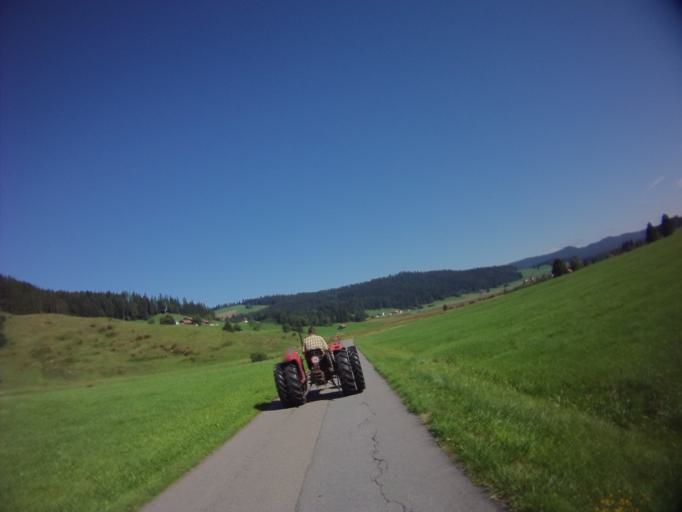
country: CH
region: Schwyz
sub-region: Bezirk Schwyz
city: Rothenthurm
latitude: 47.1122
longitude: 8.6701
